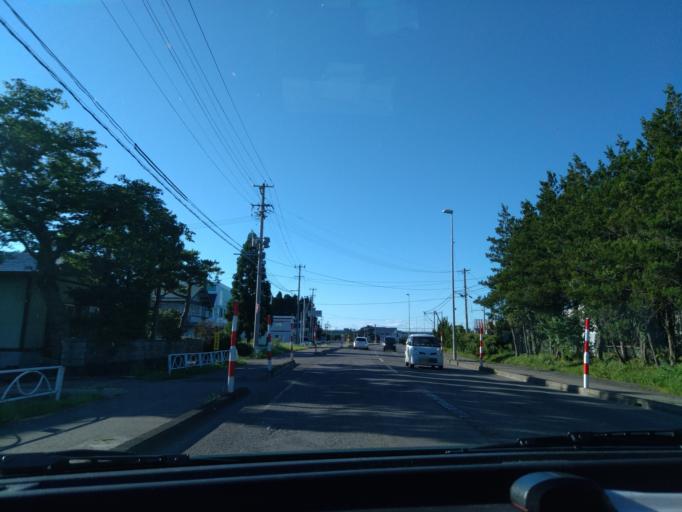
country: JP
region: Akita
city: Omagari
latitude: 39.4334
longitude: 140.4841
